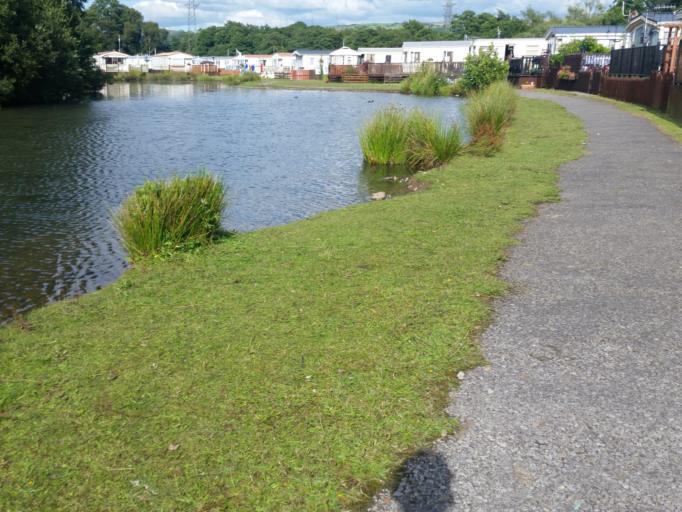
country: GB
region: Wales
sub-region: City and County of Swansea
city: Clydach
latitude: 51.6745
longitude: -3.9089
